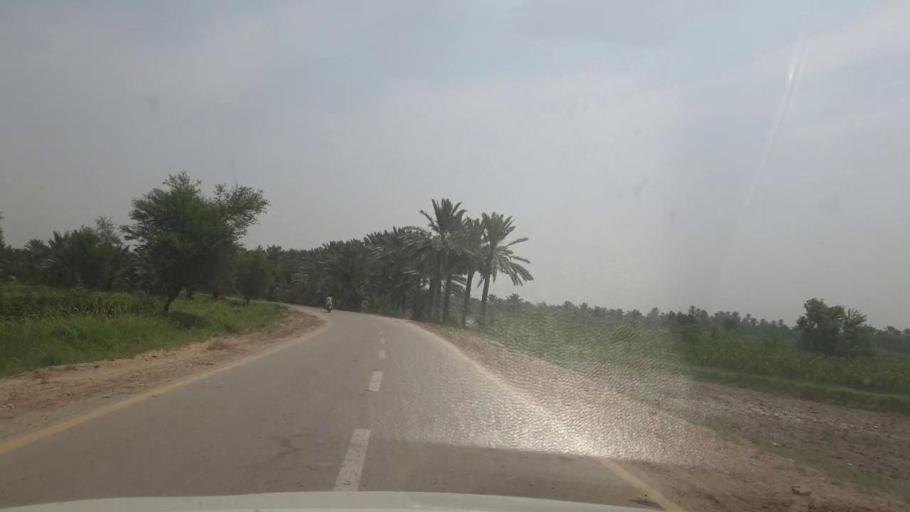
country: PK
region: Sindh
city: Kot Diji
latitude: 27.3889
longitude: 68.6587
